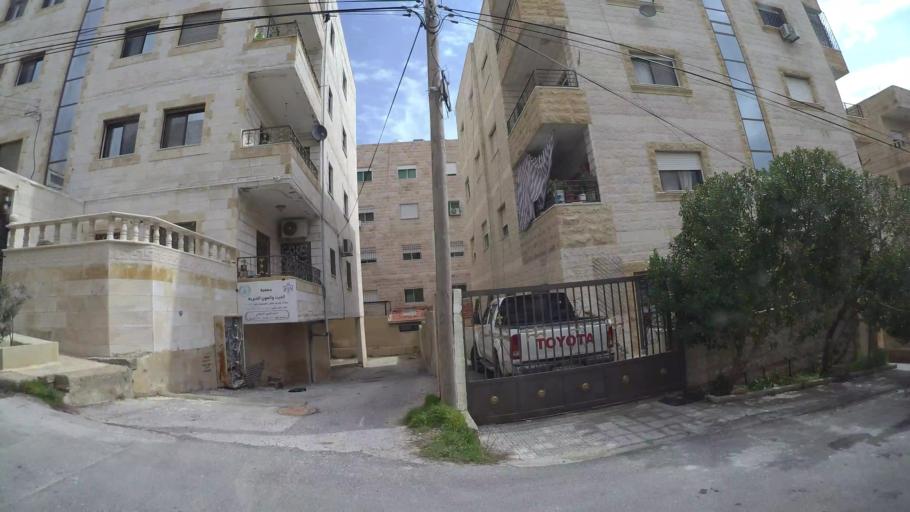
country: JO
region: Amman
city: Amman
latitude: 31.9898
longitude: 35.9217
